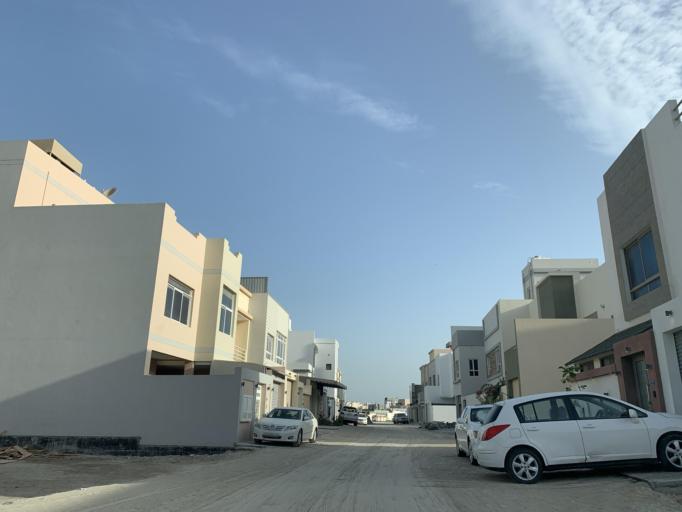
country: BH
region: Northern
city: Madinat `Isa
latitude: 26.1773
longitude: 50.5816
